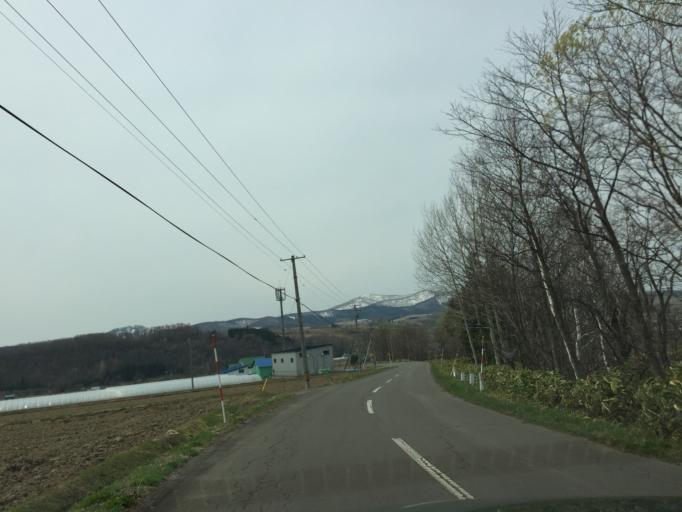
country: JP
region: Hokkaido
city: Ashibetsu
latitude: 43.6078
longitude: 142.2130
